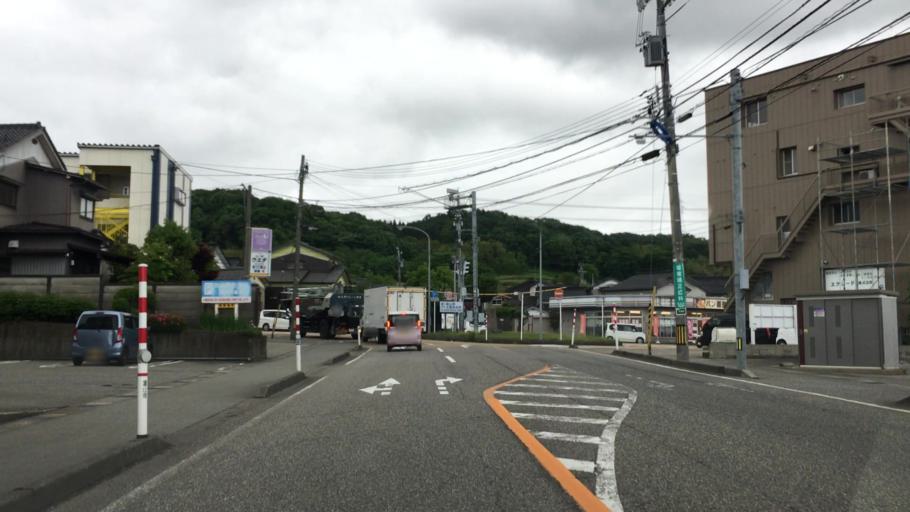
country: JP
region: Toyama
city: Toyama-shi
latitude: 36.7078
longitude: 137.1784
